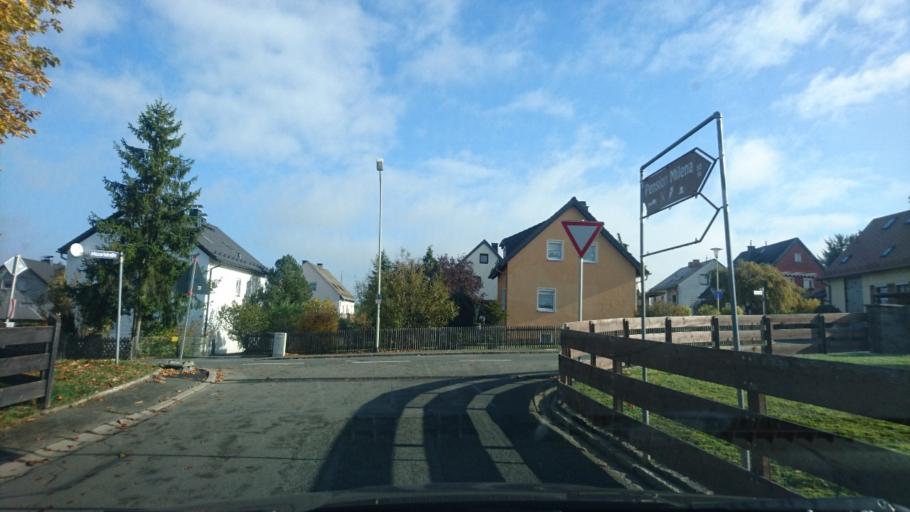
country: DE
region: Bavaria
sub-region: Upper Franconia
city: Selbitz
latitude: 50.3109
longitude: 11.7510
